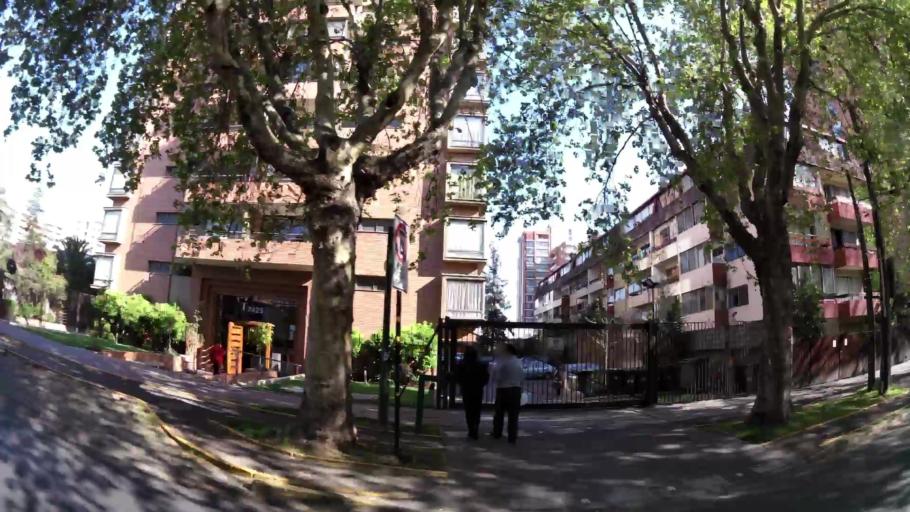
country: CL
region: Santiago Metropolitan
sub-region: Provincia de Santiago
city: Villa Presidente Frei, Nunoa, Santiago, Chile
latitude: -33.4556
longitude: -70.6062
